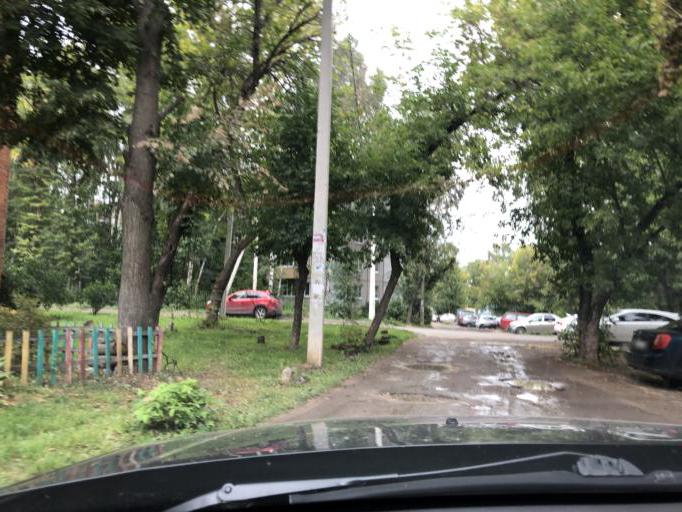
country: RU
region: Tula
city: Tula
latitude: 54.2150
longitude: 37.6676
